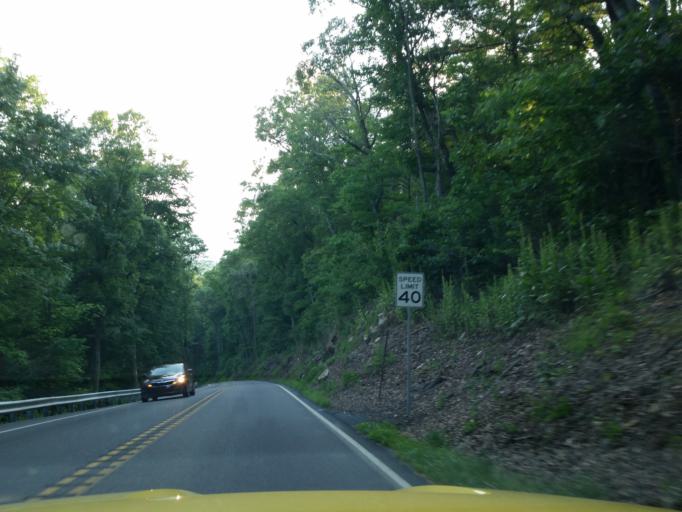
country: US
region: Pennsylvania
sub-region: Lebanon County
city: Jonestown
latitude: 40.4506
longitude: -76.6018
